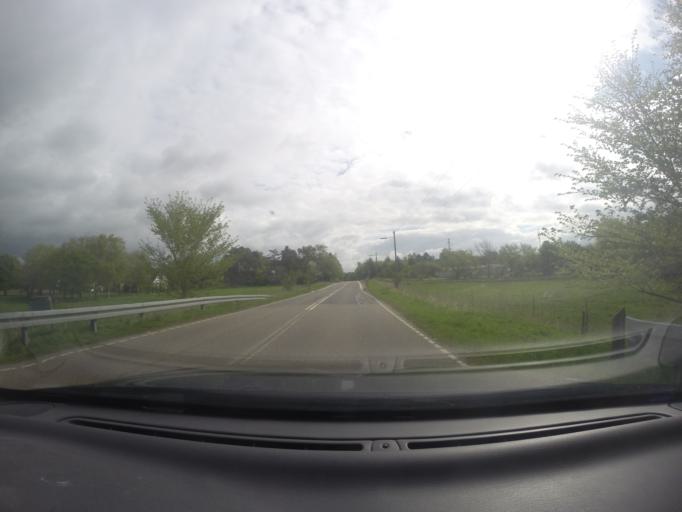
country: DK
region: Capital Region
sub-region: Hoje-Taastrup Kommune
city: Taastrup
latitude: 55.6796
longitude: 12.3214
